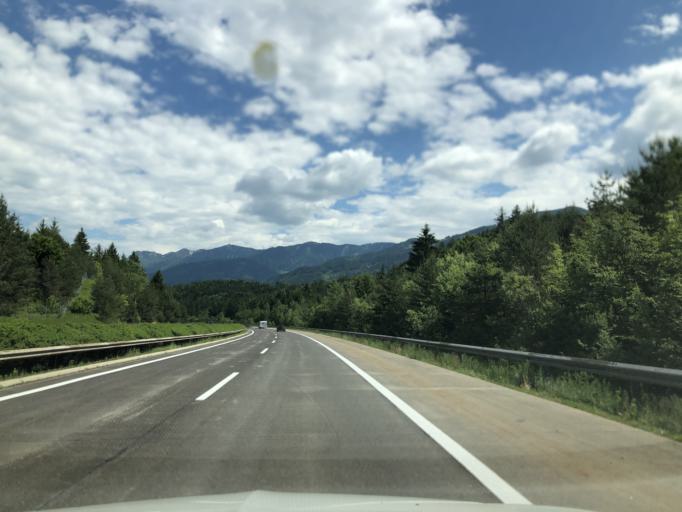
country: AT
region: Carinthia
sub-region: Politischer Bezirk Villach Land
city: Arnoldstein
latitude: 46.5597
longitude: 13.7463
